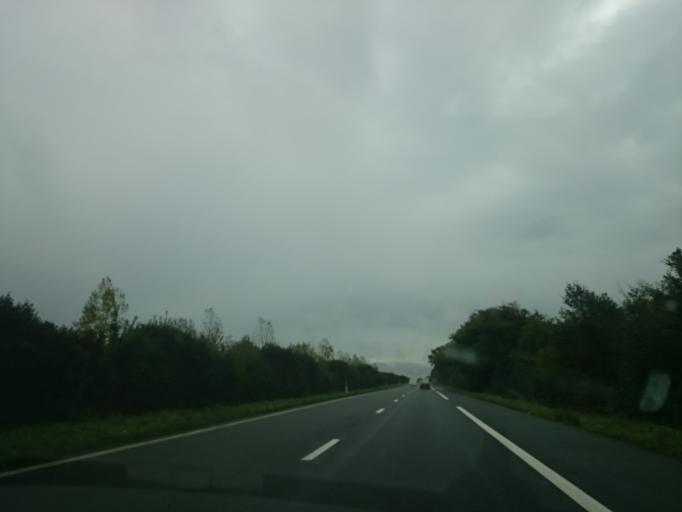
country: FR
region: Pays de la Loire
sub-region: Departement de la Loire-Atlantique
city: La Chapelle-Launay
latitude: 47.3895
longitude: -1.9872
